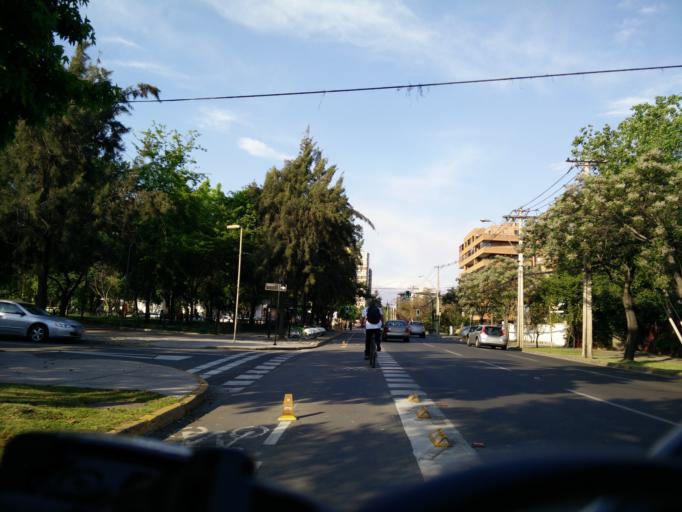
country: CL
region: Santiago Metropolitan
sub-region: Provincia de Santiago
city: Villa Presidente Frei, Nunoa, Santiago, Chile
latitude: -33.4276
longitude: -70.5790
